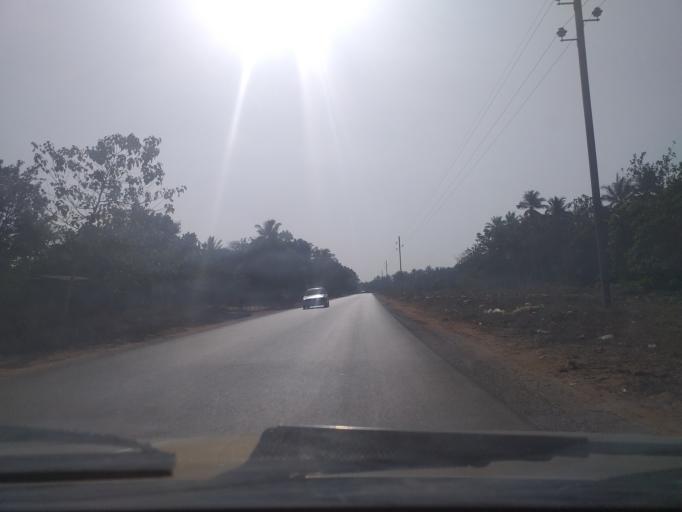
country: GN
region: Boke
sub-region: Boke Prefecture
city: Sangueya
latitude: 10.7784
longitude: -14.4434
